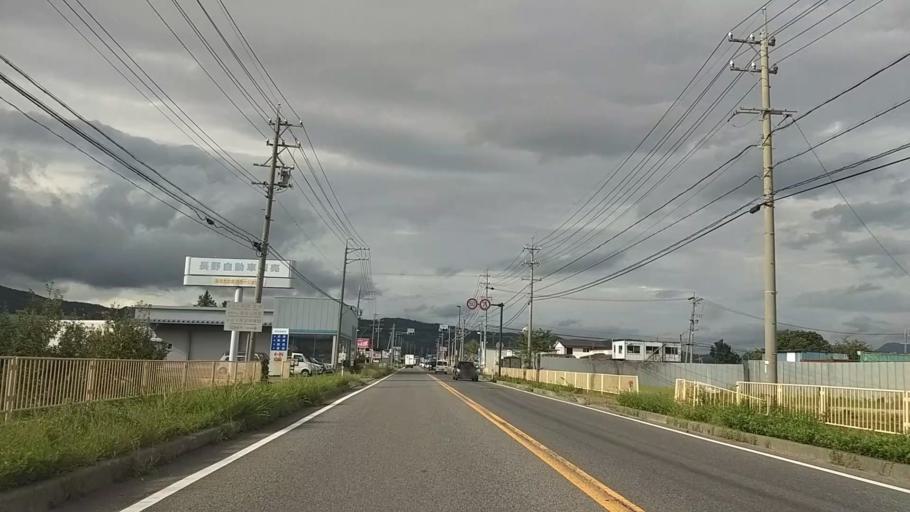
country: JP
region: Nagano
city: Suzaka
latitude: 36.6866
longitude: 138.2680
